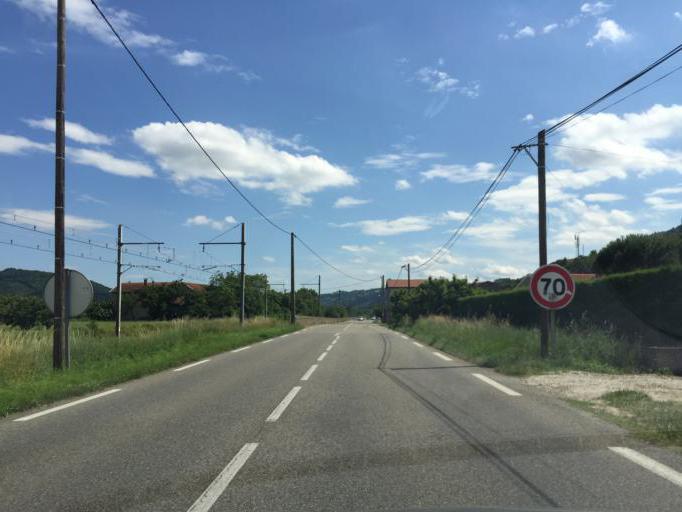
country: FR
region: Rhone-Alpes
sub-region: Departement de l'Ardeche
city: Sarras
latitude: 45.2112
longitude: 4.8032
